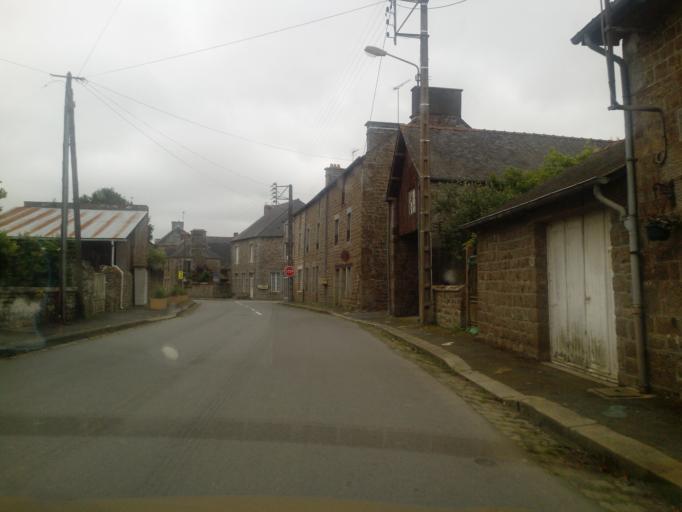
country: FR
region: Brittany
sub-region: Departement d'Ille-et-Vilaine
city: Sens-de-Bretagne
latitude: 48.3417
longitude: -1.4899
